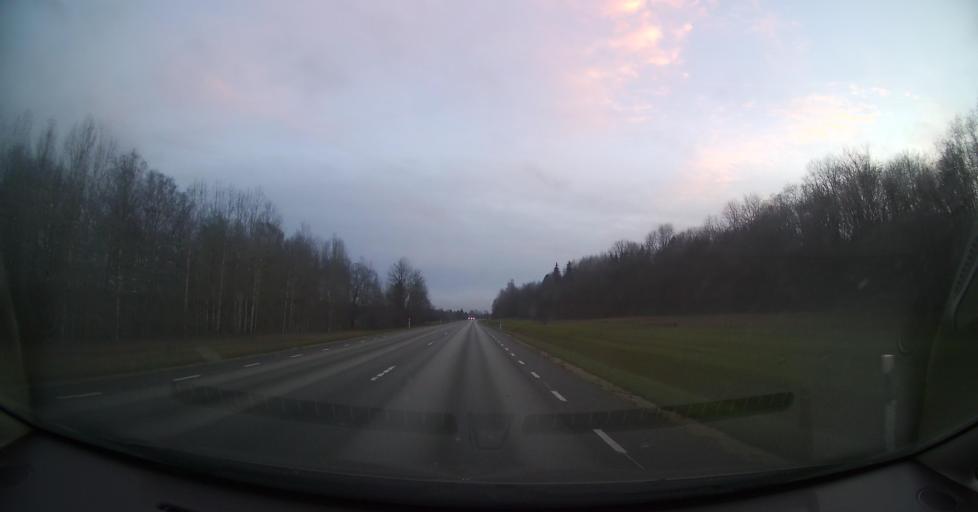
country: EE
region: Laeaene-Virumaa
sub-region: Haljala vald
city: Haljala
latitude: 59.4027
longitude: 26.3024
